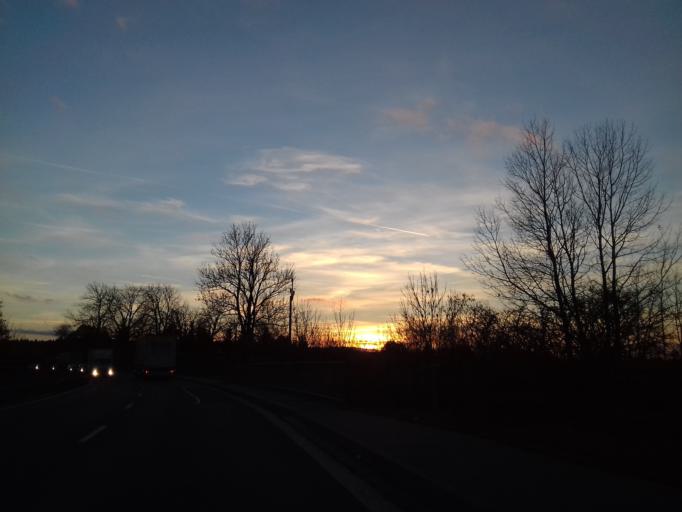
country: CZ
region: Vysocina
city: Krizova
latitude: 49.6939
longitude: 15.7991
